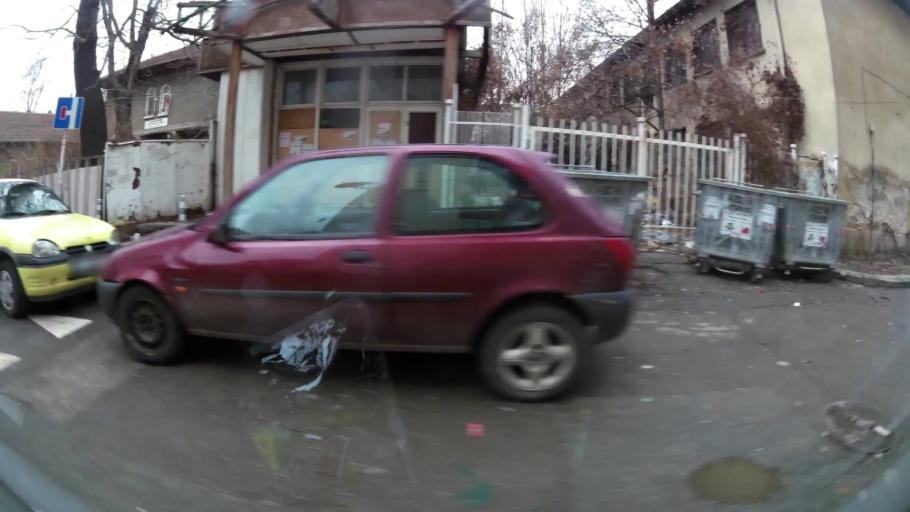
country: BG
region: Sofia-Capital
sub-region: Stolichna Obshtina
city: Sofia
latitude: 42.7267
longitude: 23.3013
